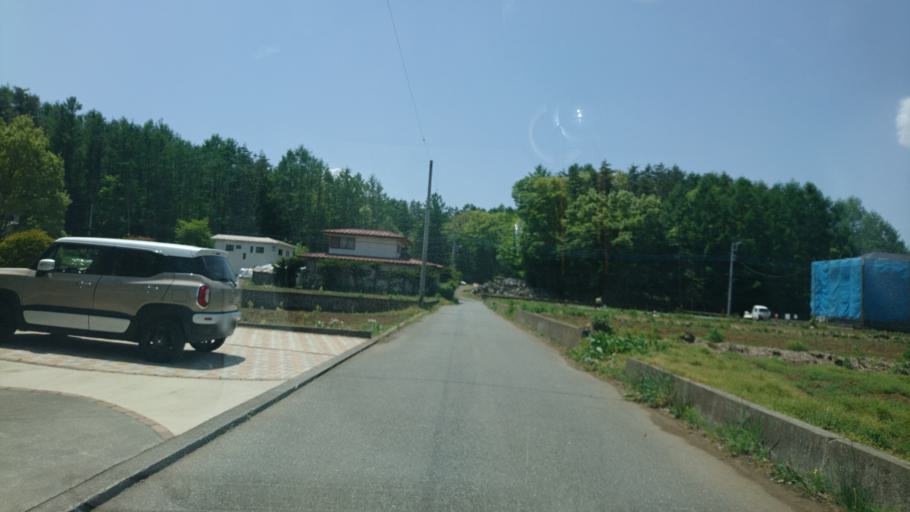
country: JP
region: Yamanashi
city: Fujikawaguchiko
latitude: 35.4938
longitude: 138.7401
